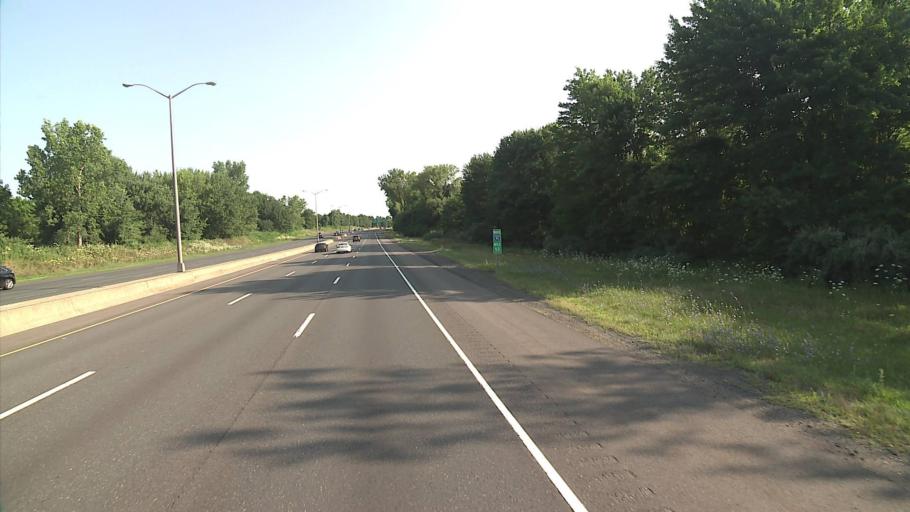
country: US
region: Connecticut
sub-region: Hartford County
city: Enfield
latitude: 41.9816
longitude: -72.5879
